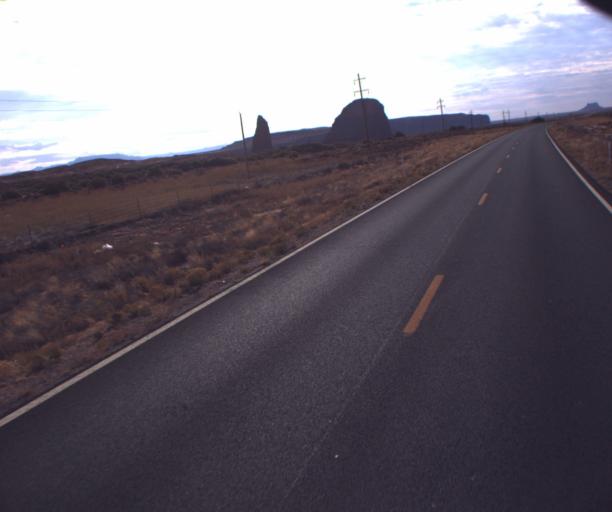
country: US
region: Arizona
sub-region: Apache County
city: Many Farms
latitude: 36.6798
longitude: -109.6027
